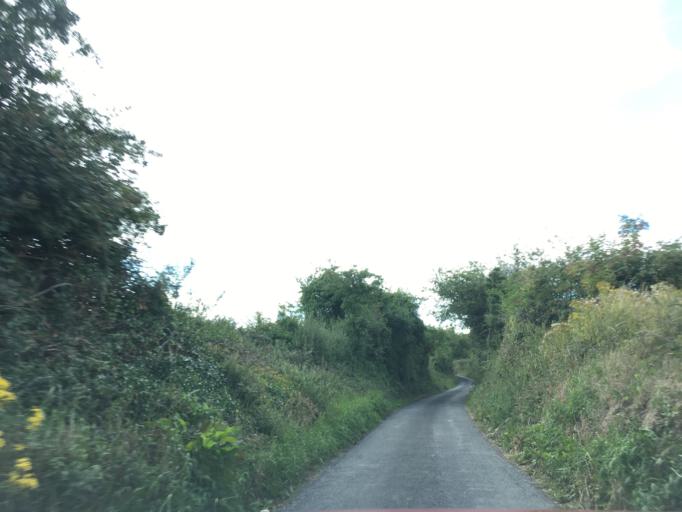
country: IE
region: Munster
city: Cashel
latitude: 52.5204
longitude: -7.8764
